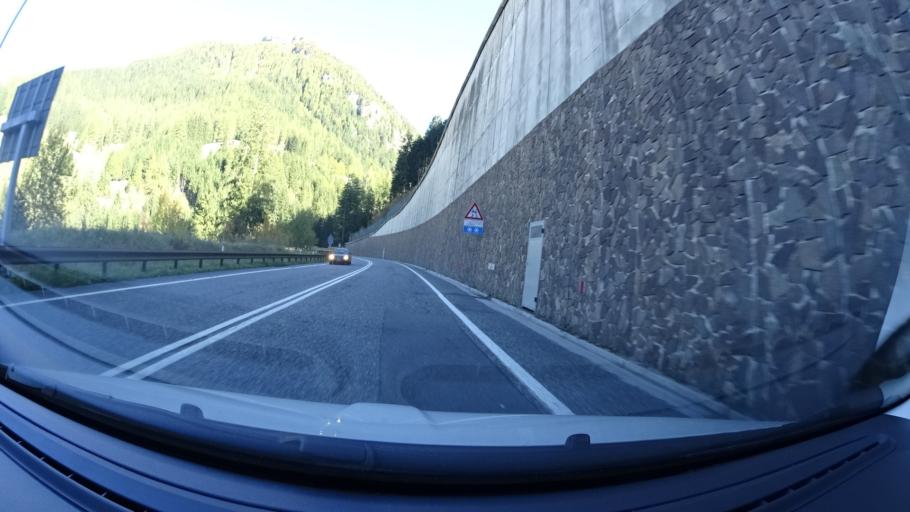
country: IT
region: Trentino-Alto Adige
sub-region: Provincia di Trento
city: Moena
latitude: 46.3743
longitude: 11.6678
